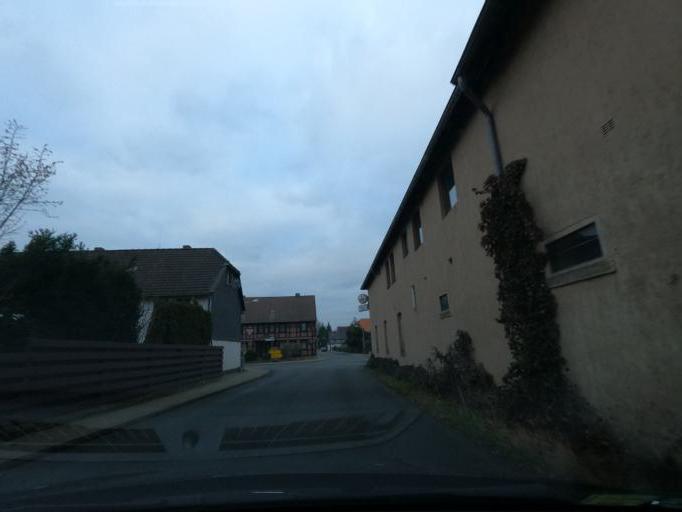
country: DE
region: Lower Saxony
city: Kissenbruck
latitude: 52.1075
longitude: 10.5914
